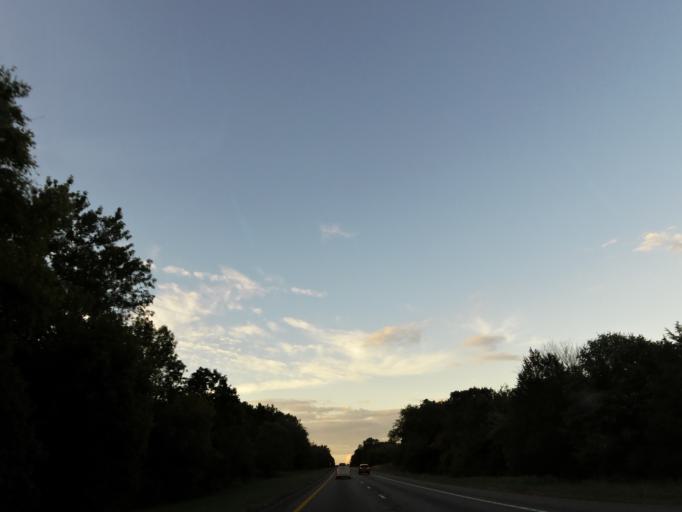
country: US
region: Tennessee
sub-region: McMinn County
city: Athens
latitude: 35.4371
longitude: -84.6780
